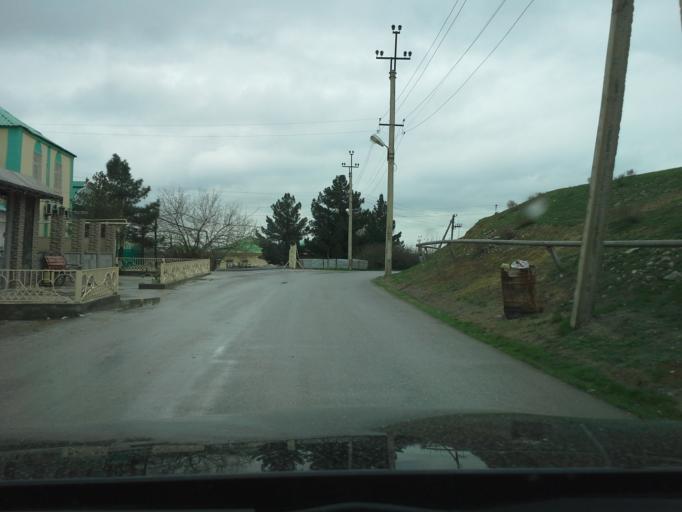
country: TM
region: Ahal
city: Abadan
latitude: 37.9524
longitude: 58.2064
